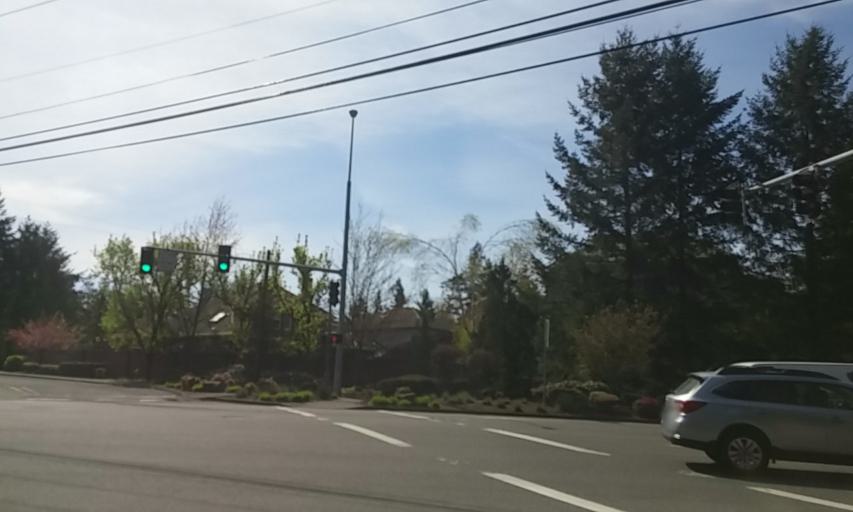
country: US
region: Oregon
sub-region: Washington County
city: West Haven-Sylvan
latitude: 45.5160
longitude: -122.7460
